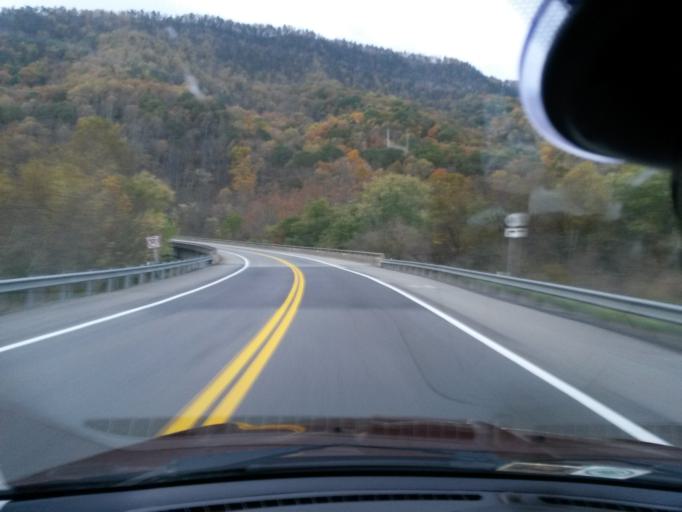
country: US
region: Virginia
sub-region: Botetourt County
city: Fincastle
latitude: 37.6470
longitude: -79.8151
